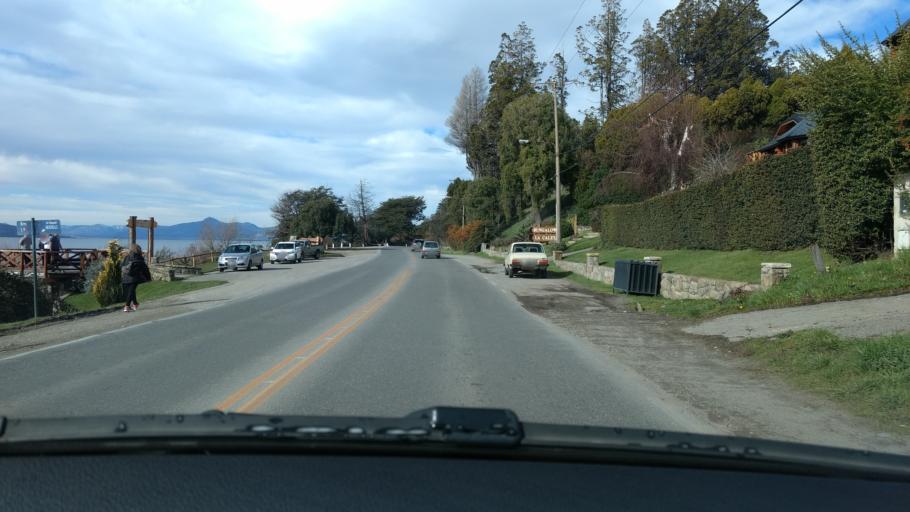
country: AR
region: Rio Negro
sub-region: Departamento de Bariloche
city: San Carlos de Bariloche
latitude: -41.1319
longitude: -71.3314
